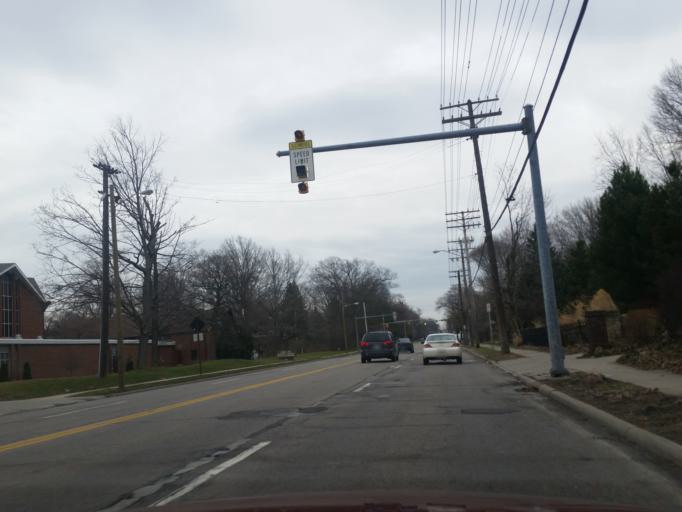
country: US
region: Ohio
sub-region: Cuyahoga County
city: East Cleveland
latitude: 41.5010
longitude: -81.5875
